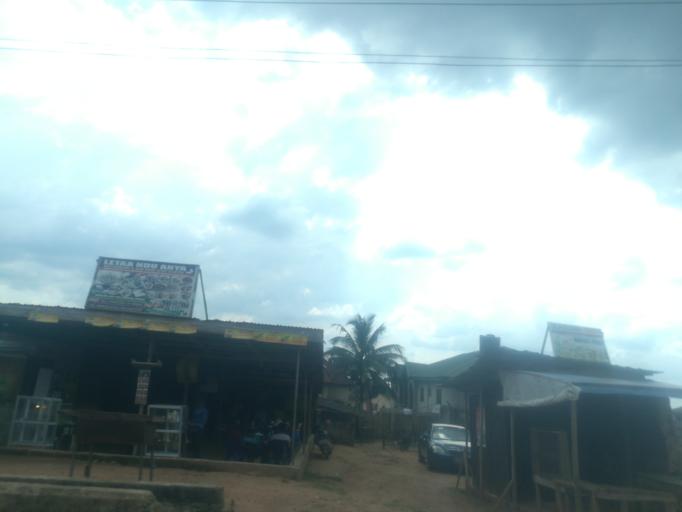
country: NG
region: Oyo
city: Ido
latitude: 7.4347
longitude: 3.8329
